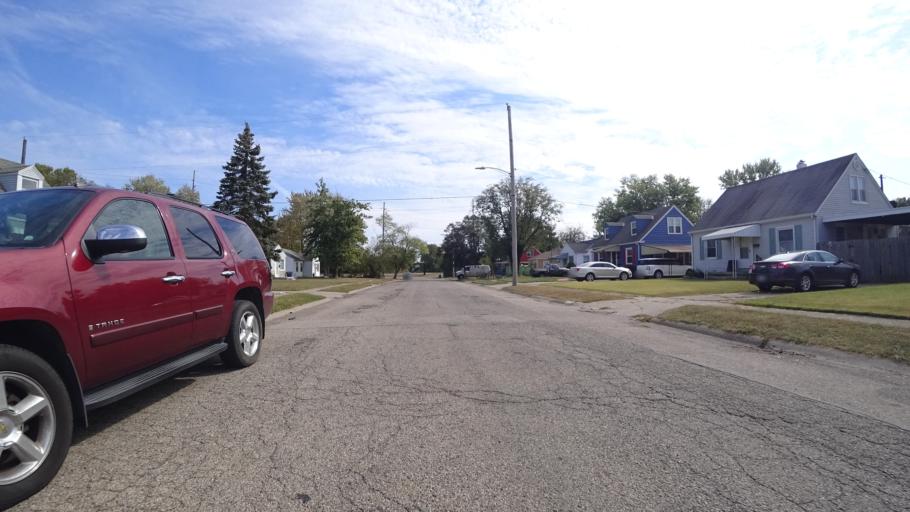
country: US
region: Ohio
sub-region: Butler County
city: Fairfield
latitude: 39.3594
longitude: -84.5438
